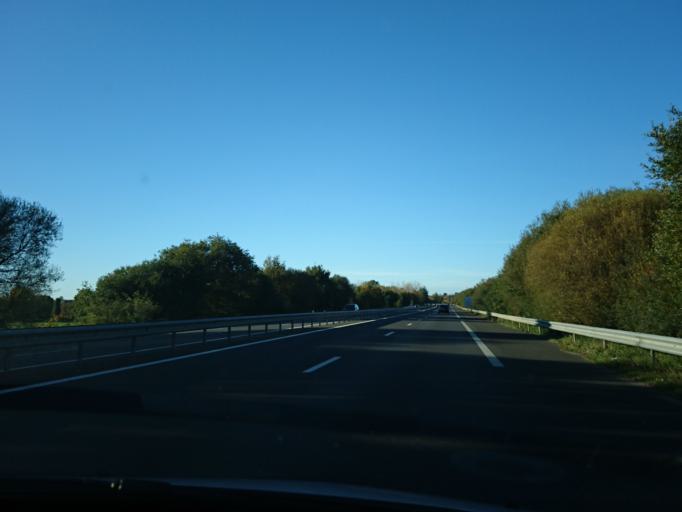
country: FR
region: Brittany
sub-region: Departement des Cotes-d'Armor
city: Broons
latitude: 48.3292
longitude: -2.2619
